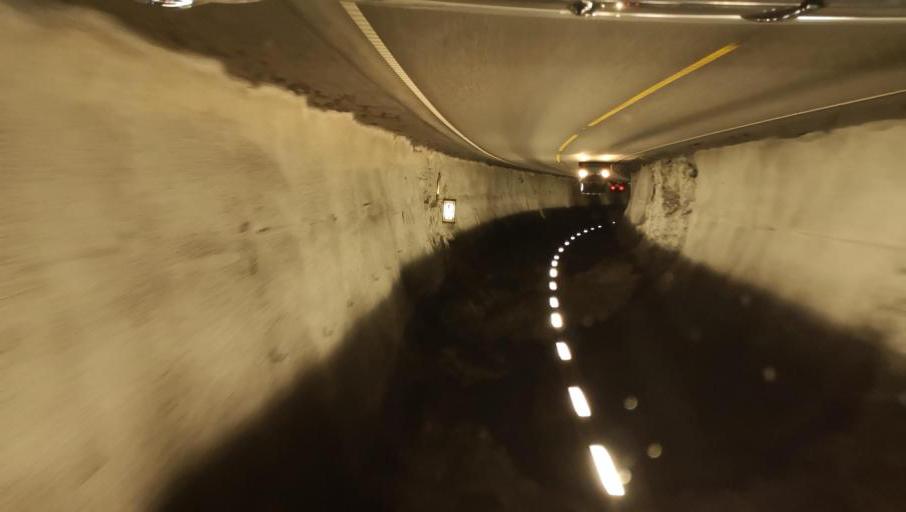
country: NO
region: Hordaland
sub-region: Granvin
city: Granvin
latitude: 60.5321
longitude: 6.7376
